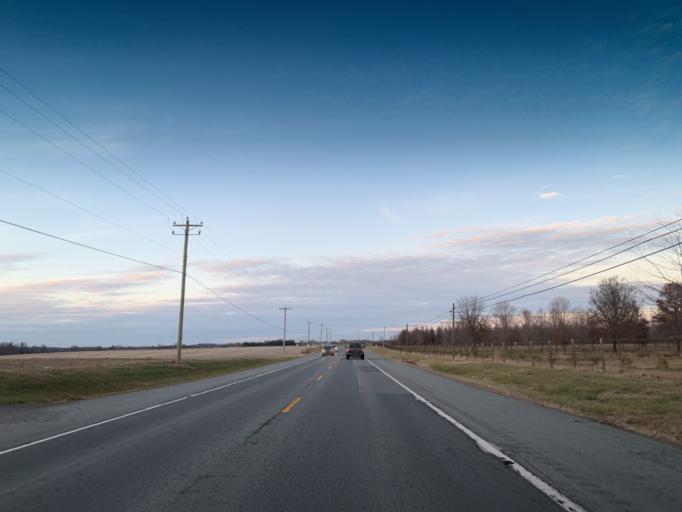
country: US
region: Delaware
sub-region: New Castle County
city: Middletown
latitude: 39.4237
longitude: -75.8602
